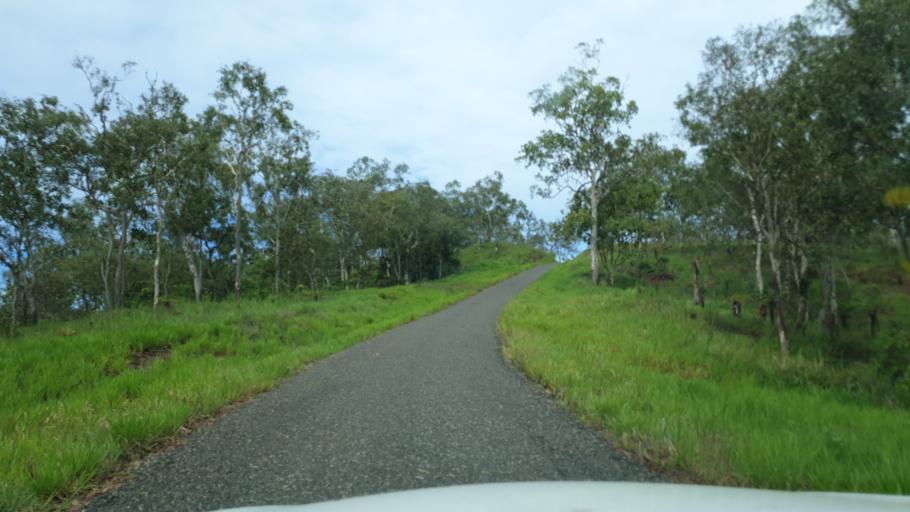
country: PG
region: National Capital
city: Port Moresby
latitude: -9.4350
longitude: 147.3793
